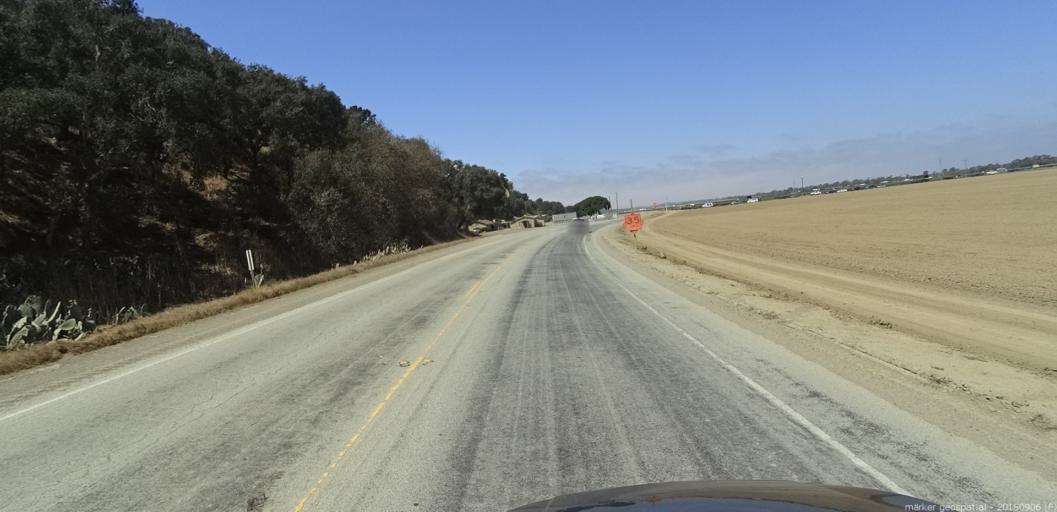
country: US
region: California
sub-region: Monterey County
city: Salinas
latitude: 36.6429
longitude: -121.7143
